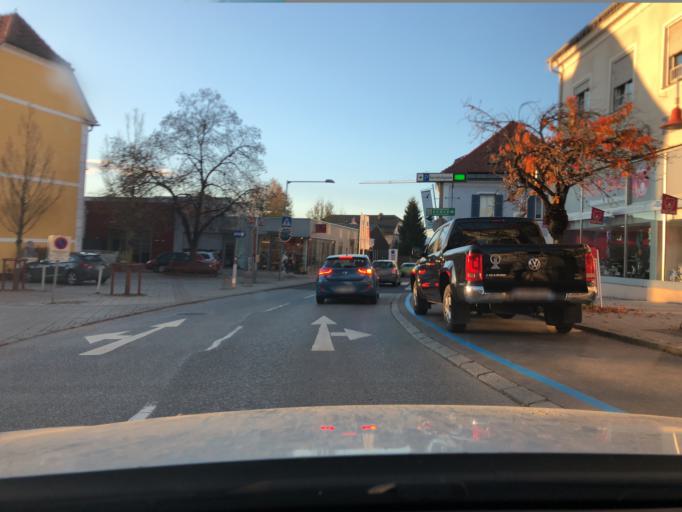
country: AT
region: Styria
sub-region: Politischer Bezirk Weiz
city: Gleisdorf
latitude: 47.1060
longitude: 15.7105
